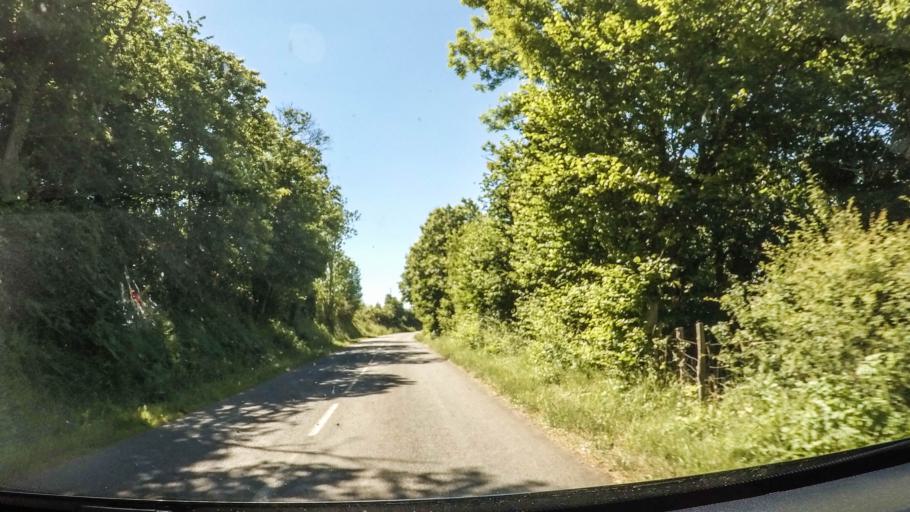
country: FR
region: Midi-Pyrenees
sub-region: Departement de l'Aveyron
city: Saint-Christophe-Vallon
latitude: 44.4726
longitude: 2.3597
